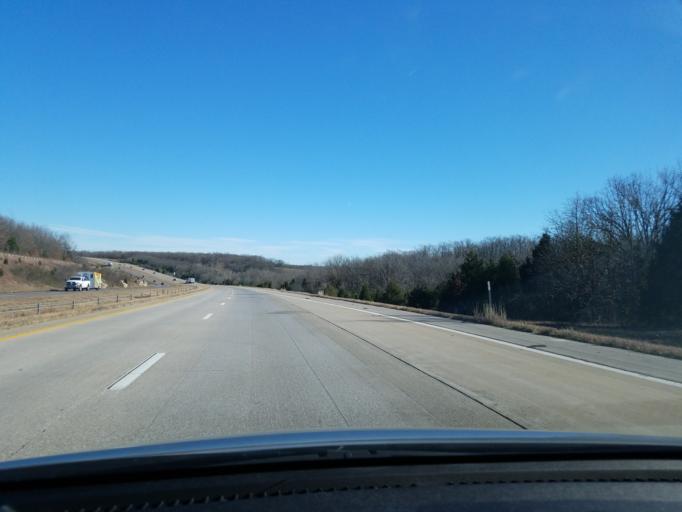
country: US
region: Missouri
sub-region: Pulaski County
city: Richland
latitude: 37.7536
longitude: -92.4997
